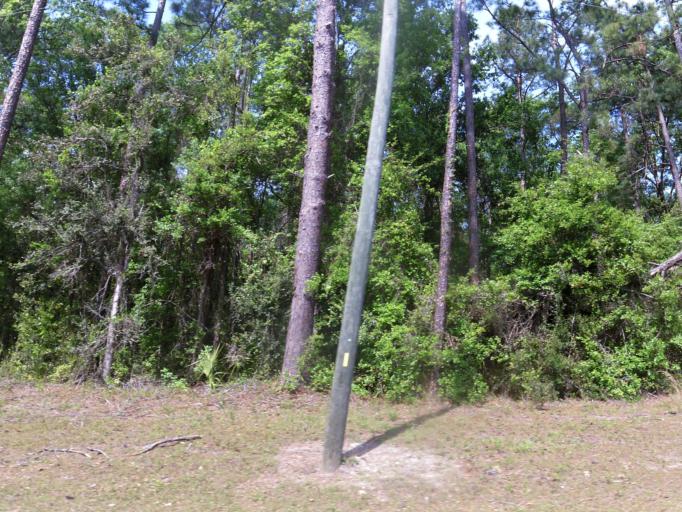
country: US
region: Georgia
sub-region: Camden County
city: Kingsland
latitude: 30.8026
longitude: -81.7349
